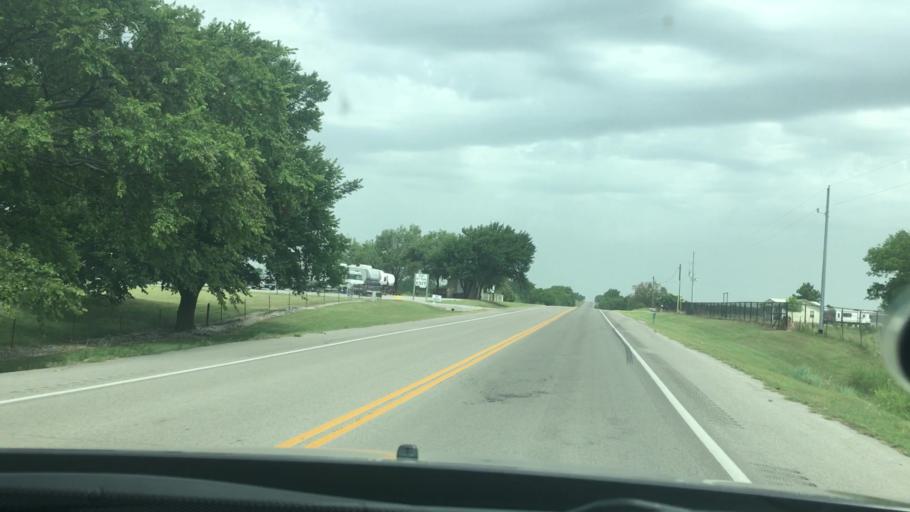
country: US
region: Oklahoma
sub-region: Garvin County
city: Pauls Valley
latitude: 34.8463
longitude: -97.2783
